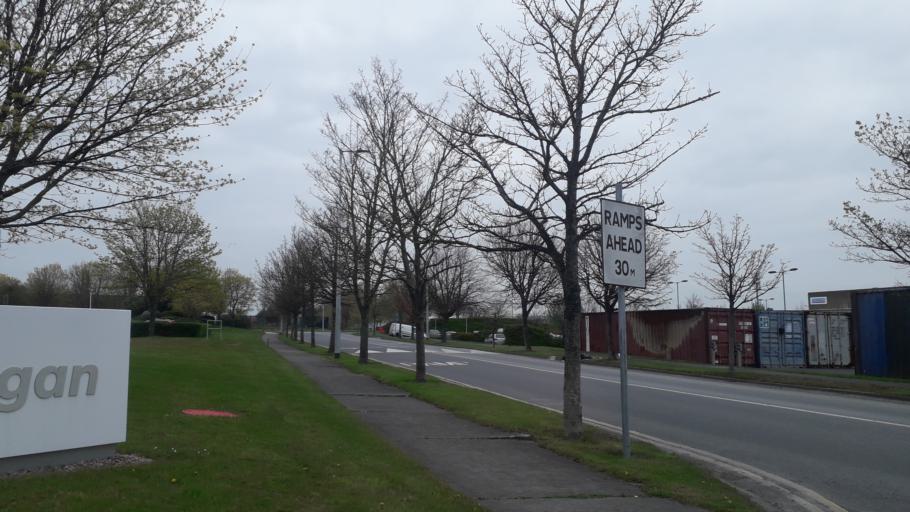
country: IE
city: Bonnybrook
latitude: 53.4028
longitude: -6.2247
